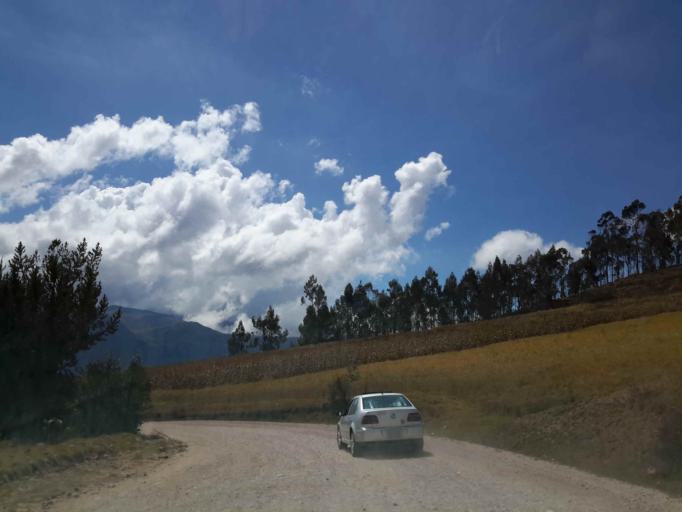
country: PE
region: Apurimac
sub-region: Provincia de Andahuaylas
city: Pacucha
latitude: -13.6319
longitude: -73.3388
